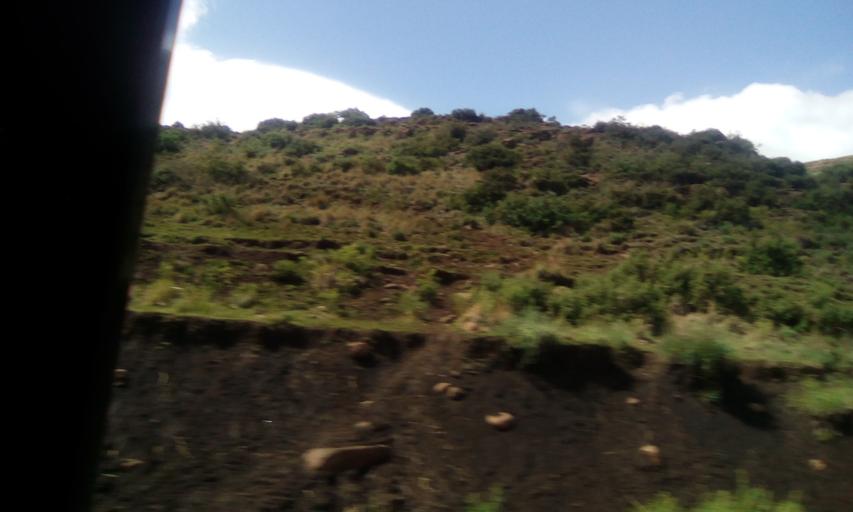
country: LS
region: Maseru
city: Nako
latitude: -29.6565
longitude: 27.8522
